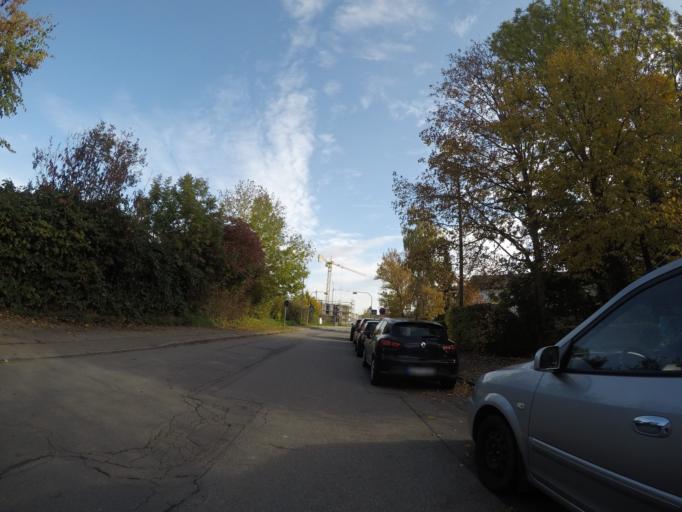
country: DE
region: Baden-Wuerttemberg
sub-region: Tuebingen Region
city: Ulm
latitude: 48.3838
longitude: 9.9617
